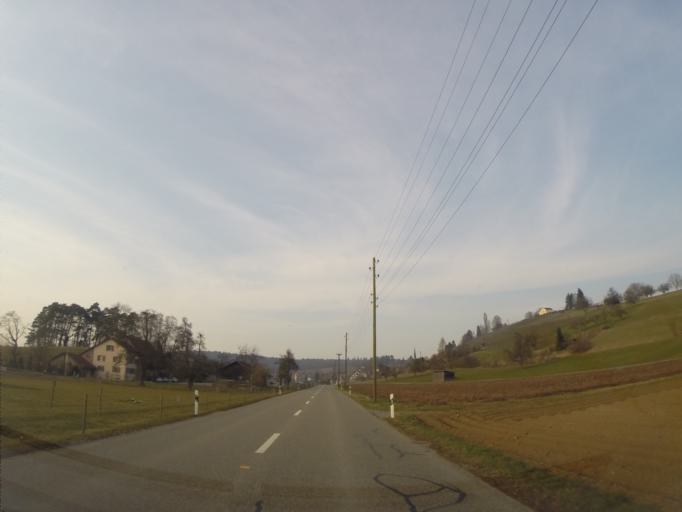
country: CH
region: Zurich
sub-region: Bezirk Andelfingen
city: Kleinandelfingen
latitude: 47.6304
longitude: 8.6926
